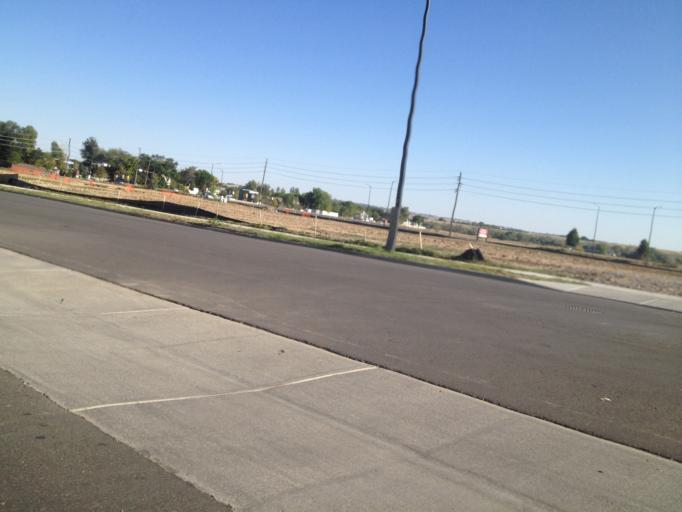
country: US
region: Colorado
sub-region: Boulder County
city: Louisville
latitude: 39.9880
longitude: -105.1214
